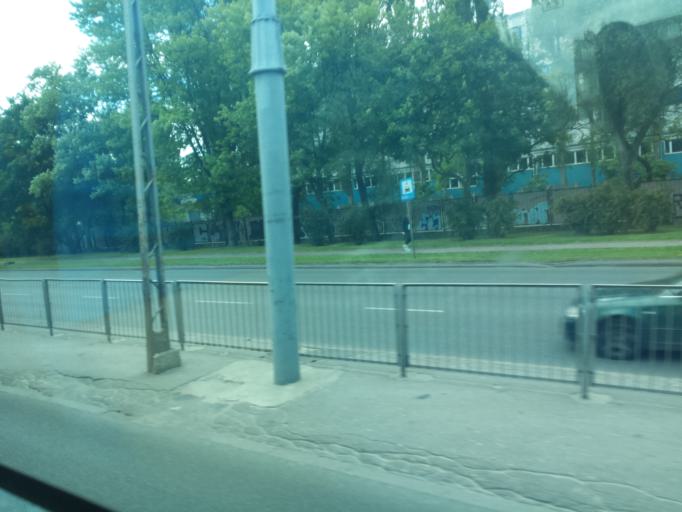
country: PL
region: Masovian Voivodeship
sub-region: Warszawa
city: Praga Poludnie
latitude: 52.2386
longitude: 21.1173
